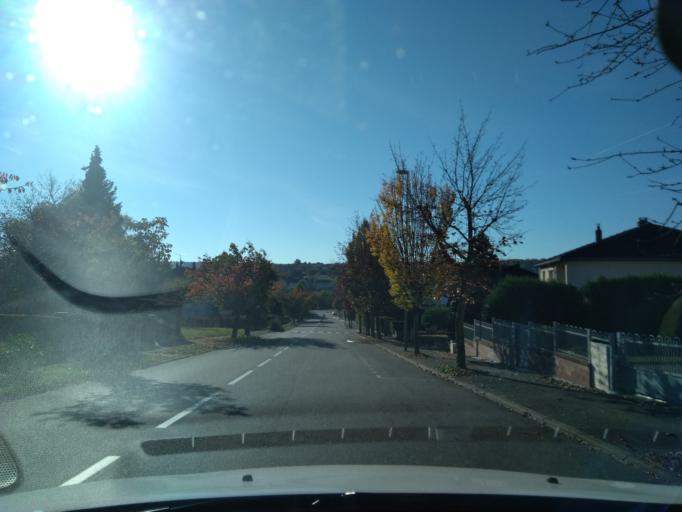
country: FR
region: Lorraine
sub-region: Departement de la Moselle
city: Sarreguemines
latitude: 49.1144
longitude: 7.0379
